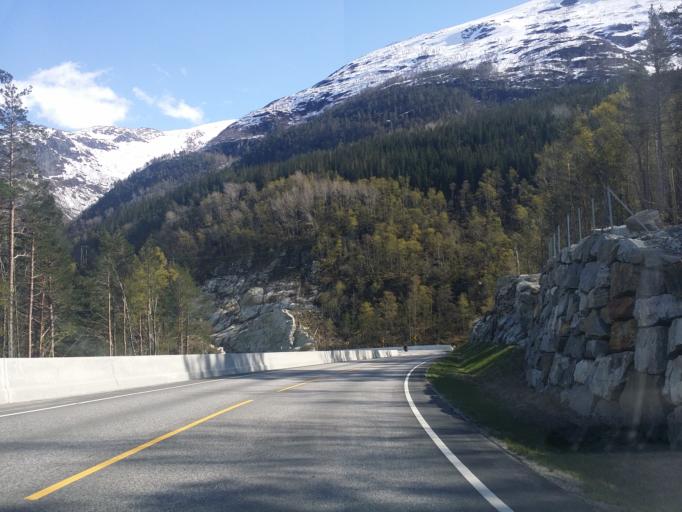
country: NO
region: Hordaland
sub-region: Ulvik
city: Ulvik
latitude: 60.4692
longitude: 6.8695
